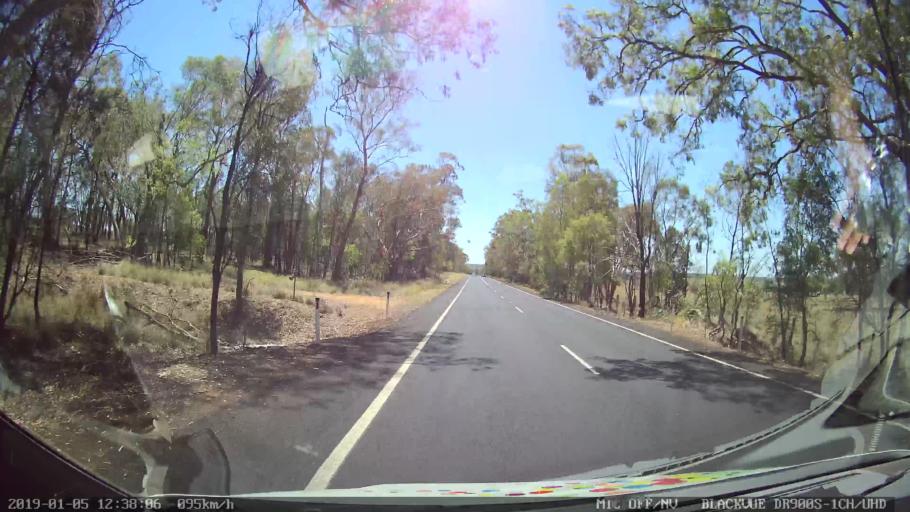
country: AU
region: New South Wales
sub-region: Warrumbungle Shire
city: Coonabarabran
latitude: -31.1983
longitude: 149.4638
